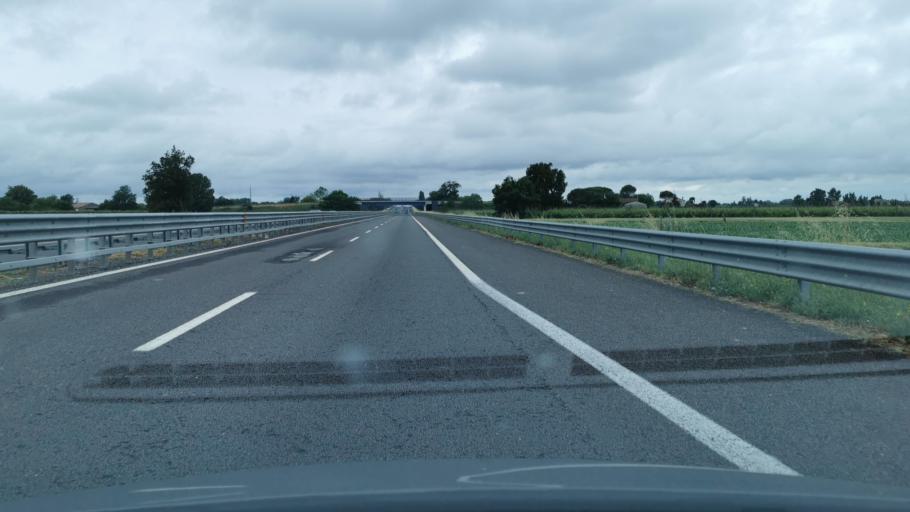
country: IT
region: Emilia-Romagna
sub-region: Provincia di Ravenna
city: Russi
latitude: 44.4035
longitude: 12.0411
